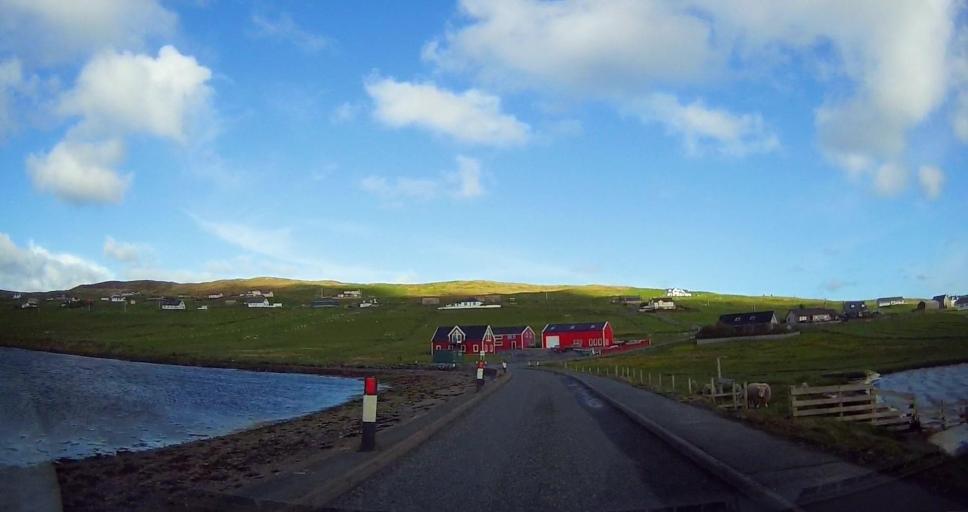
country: GB
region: Scotland
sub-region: Shetland Islands
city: Shetland
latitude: 60.3696
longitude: -1.1311
